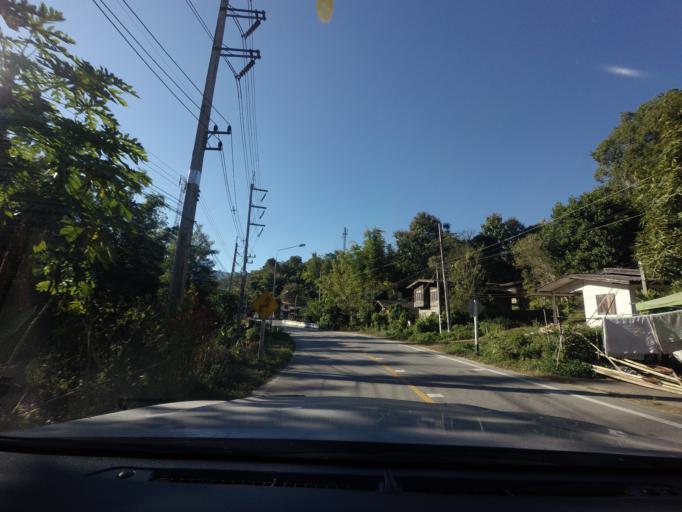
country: TH
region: Mae Hong Son
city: Mae Hi
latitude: 19.2044
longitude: 98.6715
